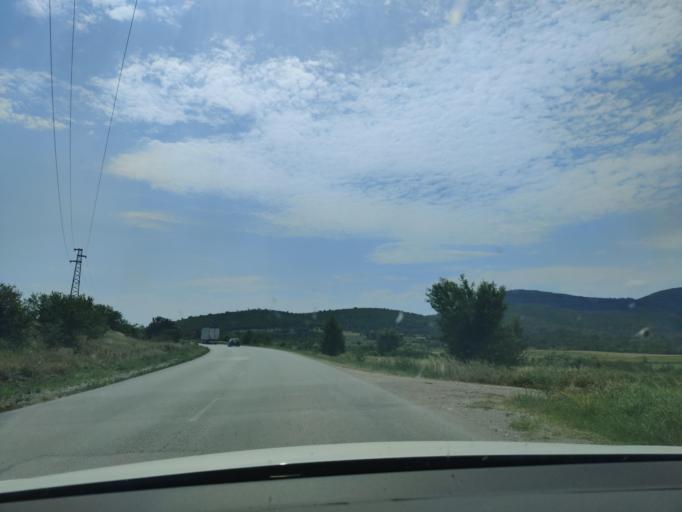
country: BG
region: Montana
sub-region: Obshtina Chiprovtsi
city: Chiprovtsi
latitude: 43.5139
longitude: 22.9784
